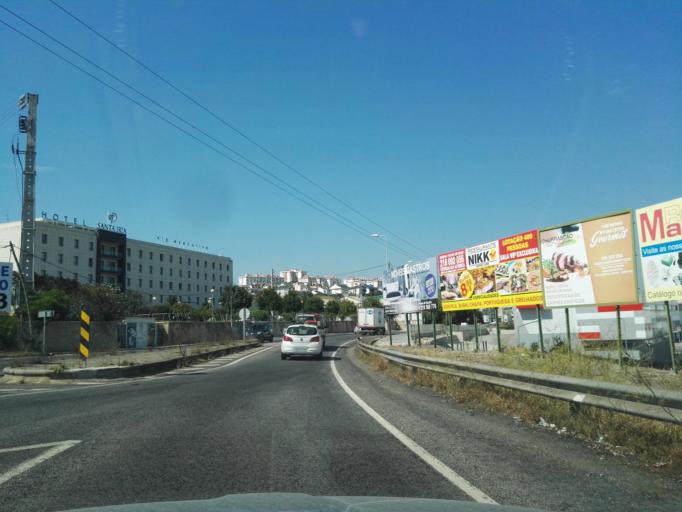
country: PT
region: Lisbon
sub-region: Loures
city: Santa Iria da Azoia
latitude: 38.8377
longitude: -9.0825
